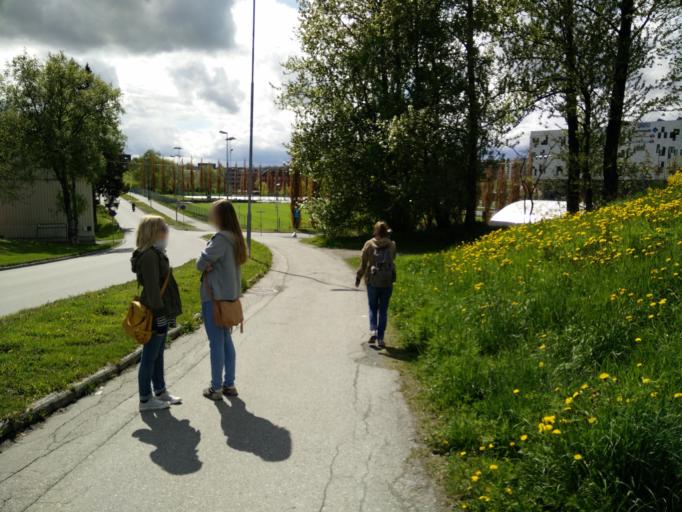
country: NO
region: Sor-Trondelag
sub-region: Trondheim
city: Trondheim
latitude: 63.4122
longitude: 10.4079
